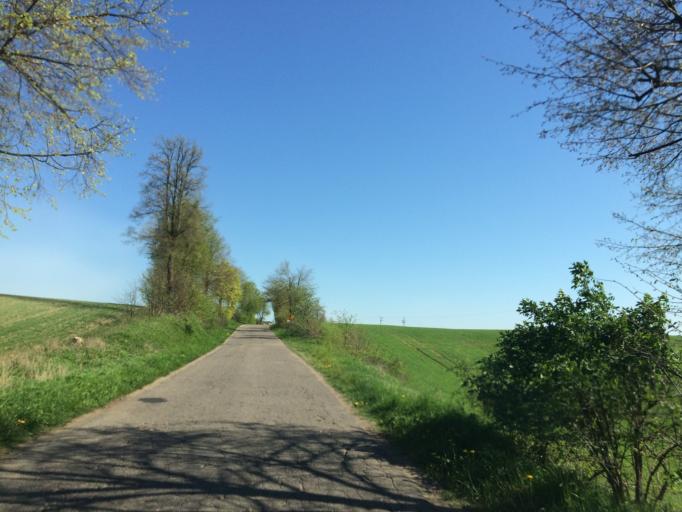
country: PL
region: Warmian-Masurian Voivodeship
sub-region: Powiat dzialdowski
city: Rybno
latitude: 53.4477
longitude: 19.9258
